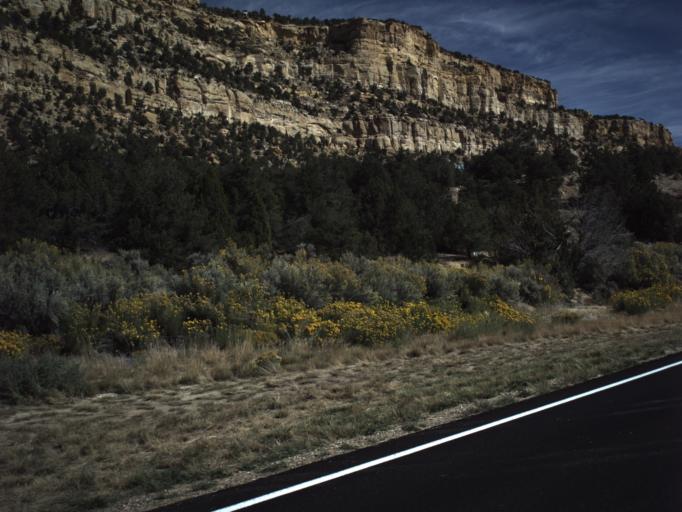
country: US
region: Utah
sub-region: Garfield County
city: Panguitch
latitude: 37.7281
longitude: -111.7677
